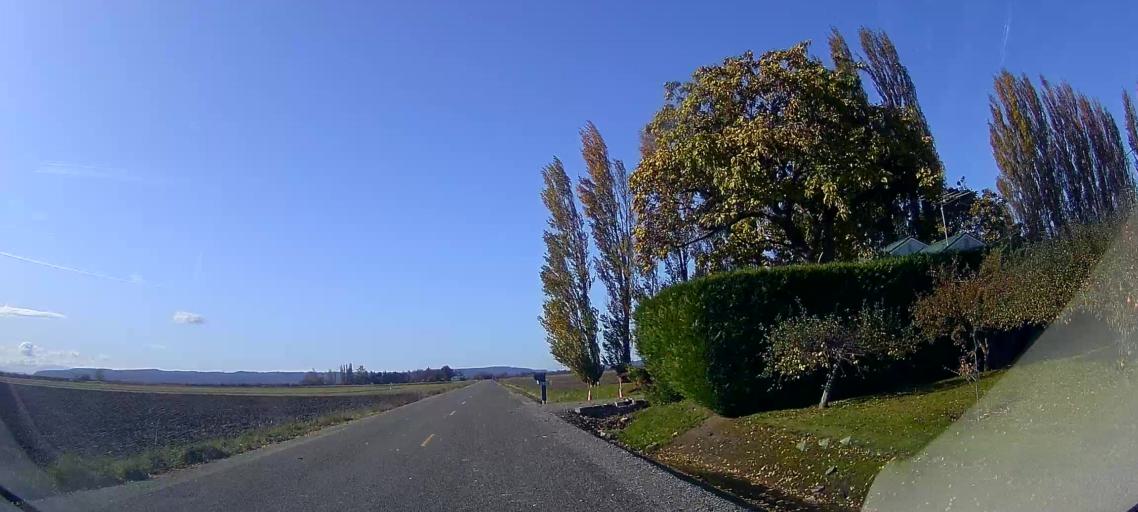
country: US
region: Washington
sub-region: Snohomish County
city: Stanwood
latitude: 48.3411
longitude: -122.4284
